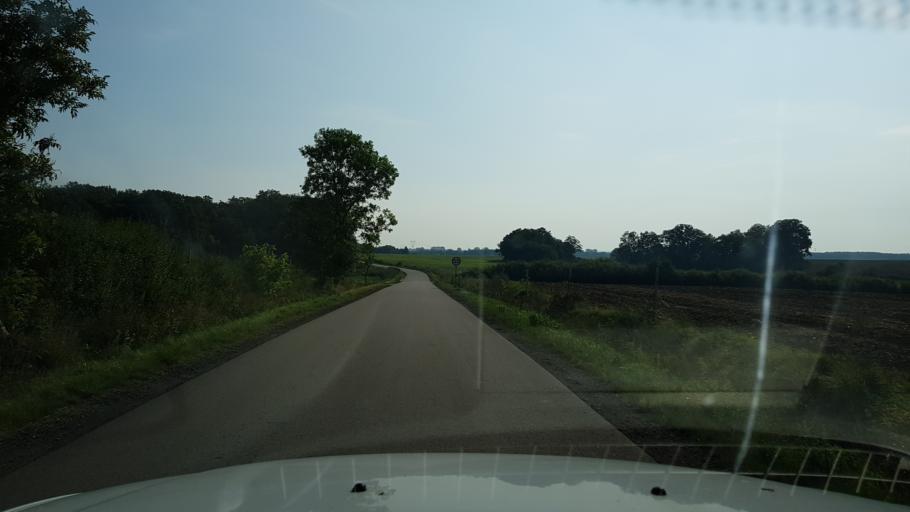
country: PL
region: West Pomeranian Voivodeship
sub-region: Powiat slawienski
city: Slawno
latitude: 54.3753
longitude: 16.6166
